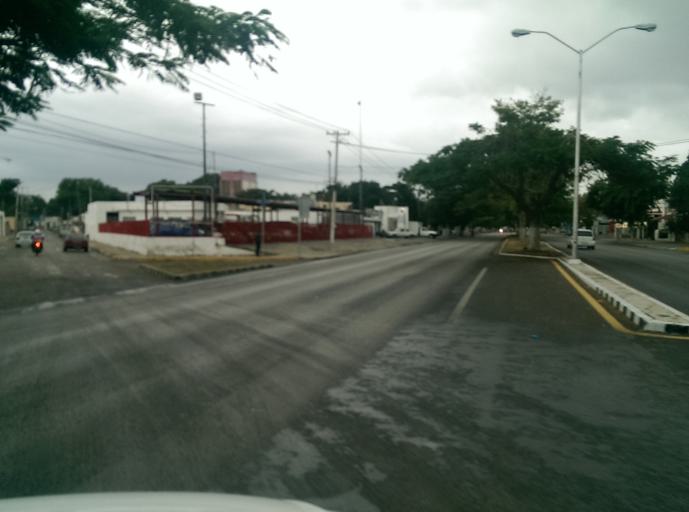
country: MX
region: Yucatan
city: Merida
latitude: 20.9807
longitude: -89.6397
